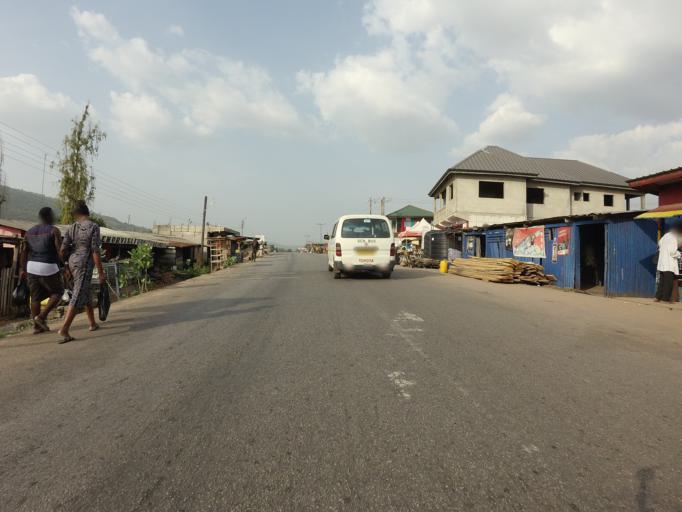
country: GH
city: Akropong
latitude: 6.2557
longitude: 0.1343
